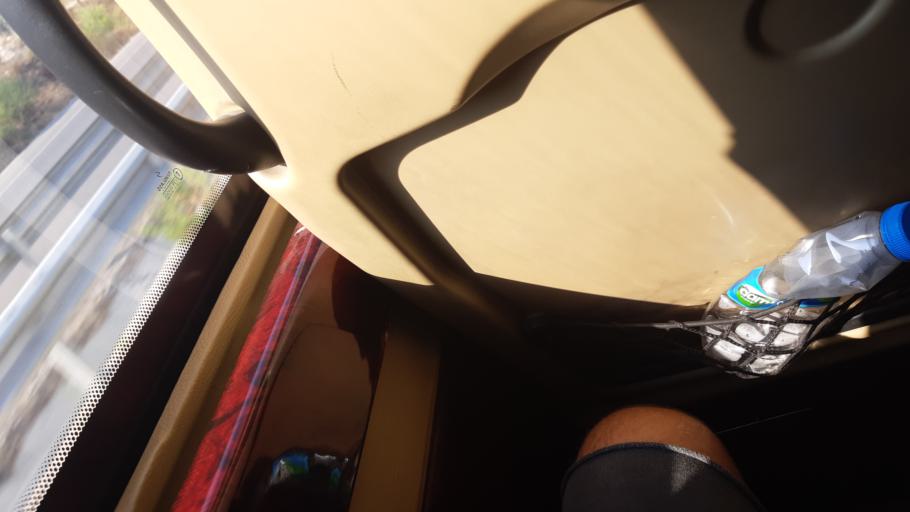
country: TR
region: Izmir
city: Urla
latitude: 38.3238
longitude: 26.7256
